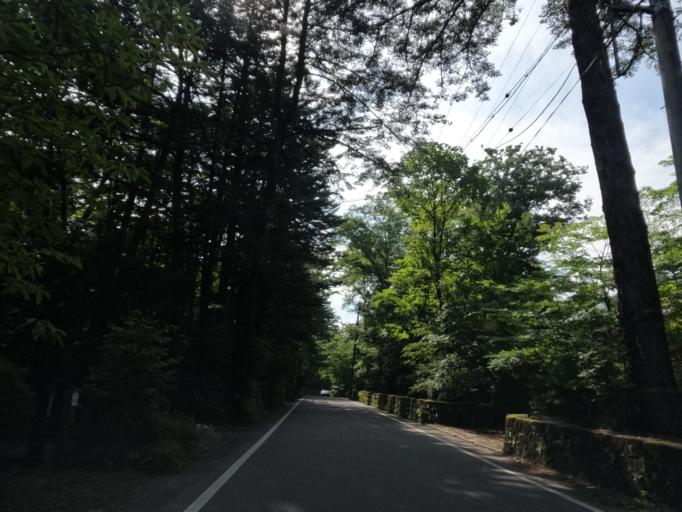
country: JP
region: Nagano
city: Komoro
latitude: 36.3585
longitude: 138.6275
